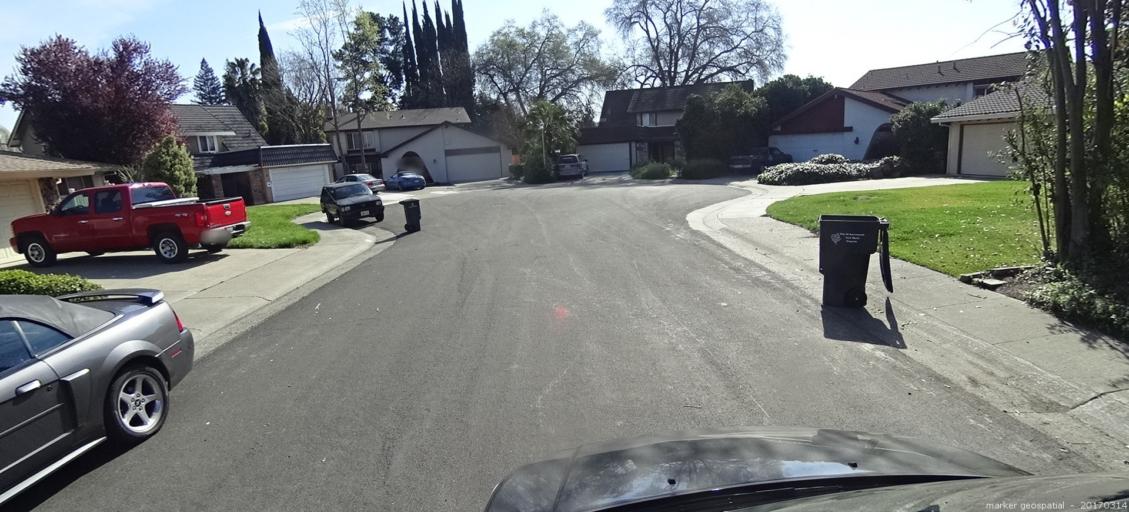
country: US
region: California
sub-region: Sacramento County
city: Parkway
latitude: 38.5035
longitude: -121.5208
